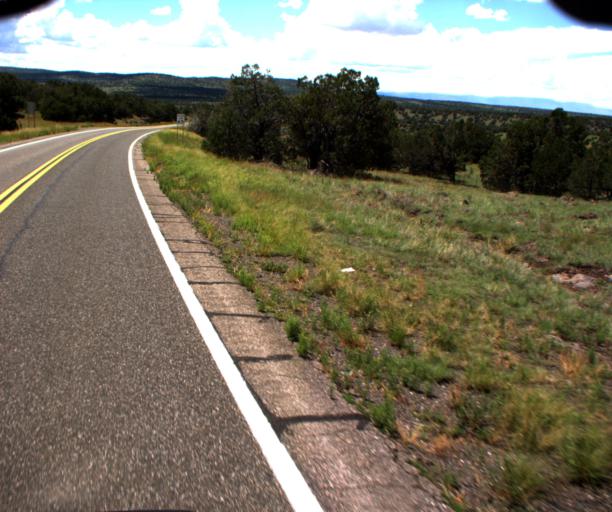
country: US
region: Arizona
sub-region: Gila County
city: Pine
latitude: 34.5097
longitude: -111.5523
